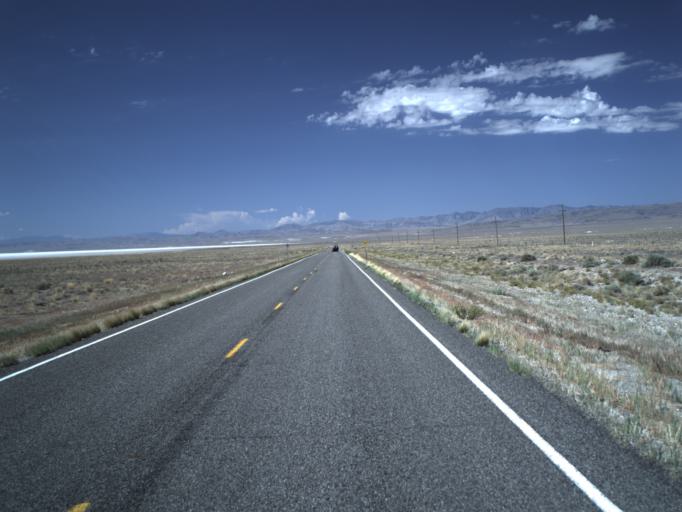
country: US
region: Utah
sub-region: Millard County
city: Delta
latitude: 39.1358
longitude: -113.0940
